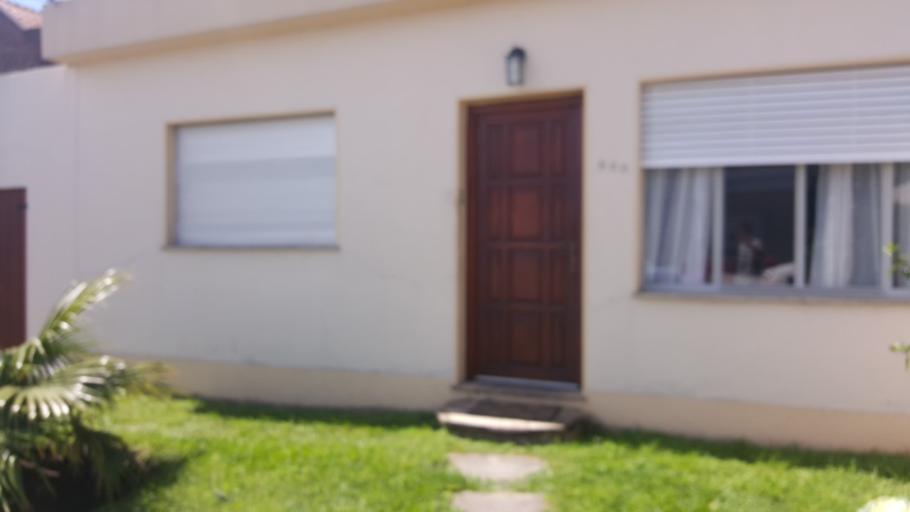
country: UY
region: Florida
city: Florida
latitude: -34.0978
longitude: -56.2212
